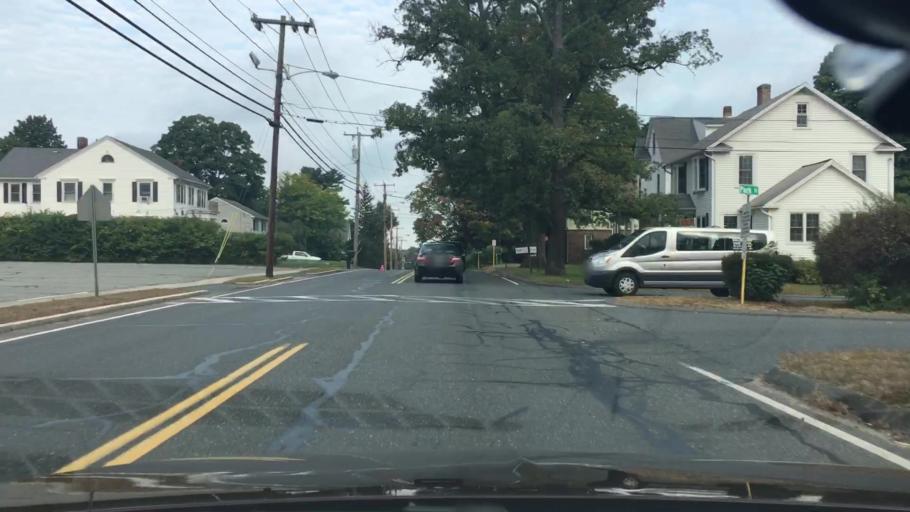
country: US
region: Massachusetts
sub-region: Hampden County
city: East Longmeadow
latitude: 42.0624
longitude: -72.5091
